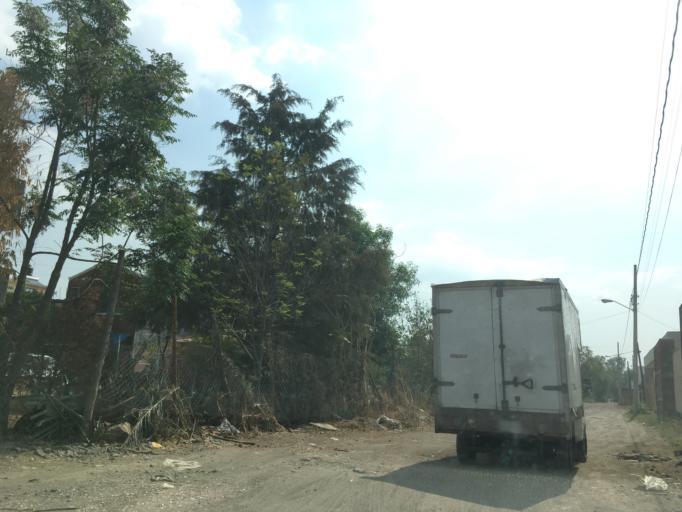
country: MX
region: Michoacan
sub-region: Morelia
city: Morelos
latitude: 19.6718
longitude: -101.2276
